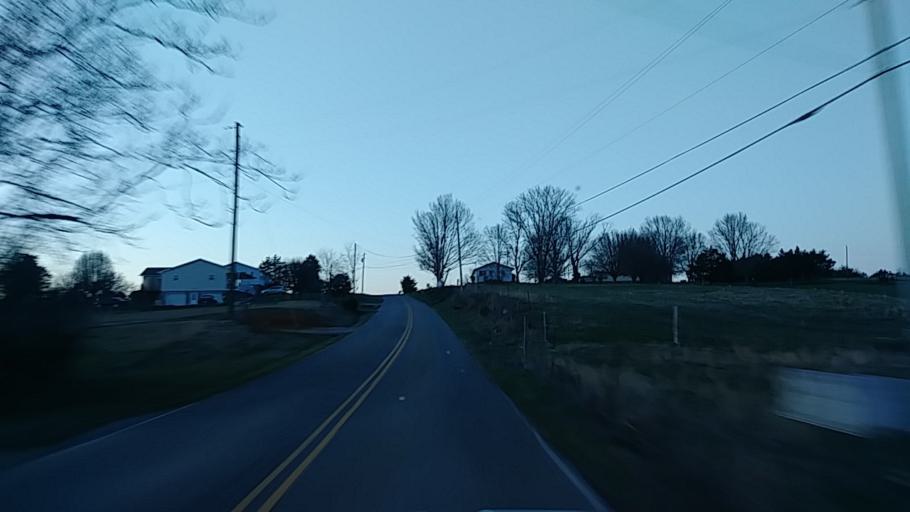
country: US
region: Tennessee
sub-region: Greene County
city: Mosheim
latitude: 36.0963
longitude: -82.9226
